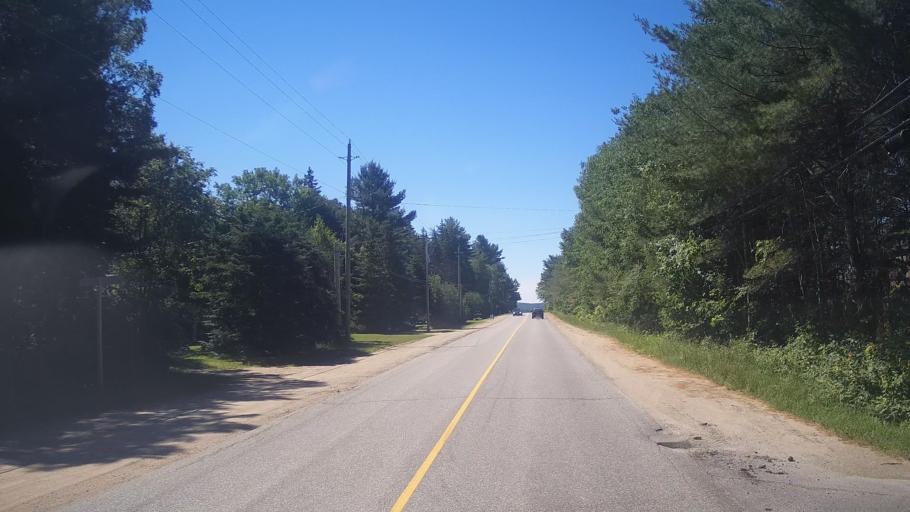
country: CA
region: Ontario
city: Huntsville
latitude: 45.3588
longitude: -79.2038
